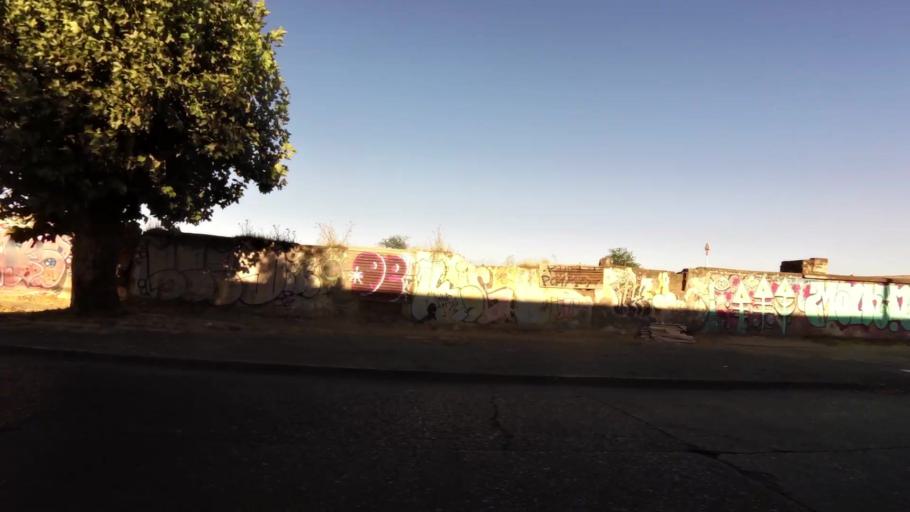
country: CL
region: Maule
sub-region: Provincia de Curico
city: Curico
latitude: -34.9804
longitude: -71.2479
